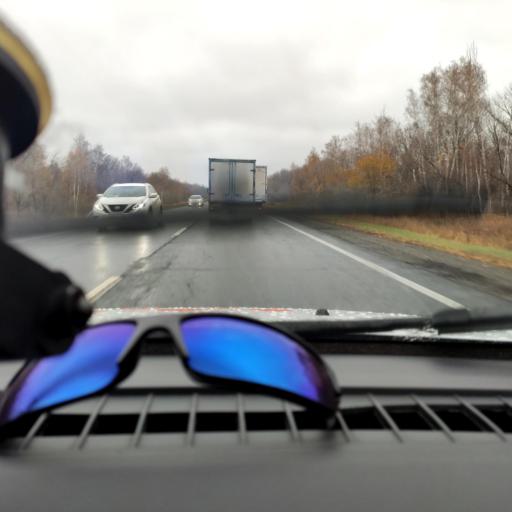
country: RU
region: Samara
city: Chapayevsk
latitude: 52.9913
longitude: 49.8408
